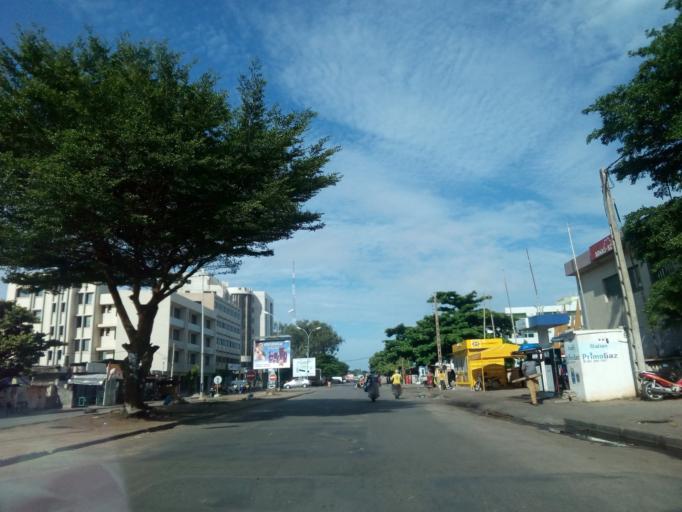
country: BJ
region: Littoral
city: Cotonou
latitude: 6.3604
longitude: 2.4213
